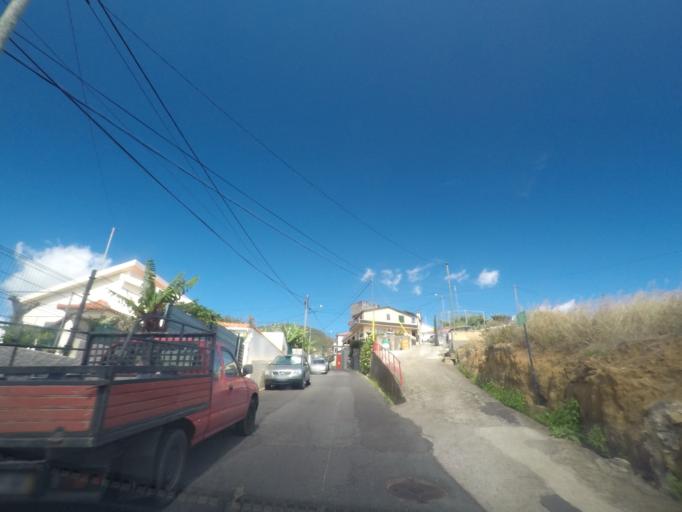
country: PT
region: Madeira
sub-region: Ribeira Brava
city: Campanario
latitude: 32.6746
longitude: -17.0505
